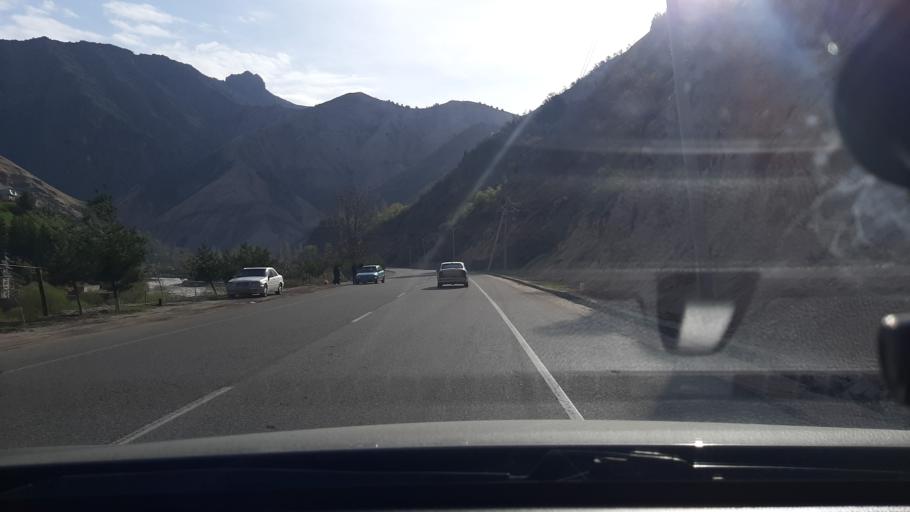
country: TJ
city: Tagob
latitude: 38.8442
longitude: 68.8379
